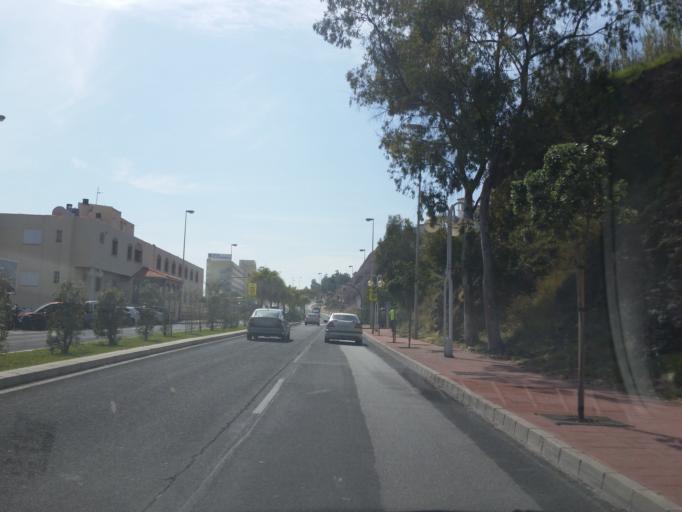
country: ES
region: Andalusia
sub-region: Provincia de Malaga
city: Benalmadena
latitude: 36.5809
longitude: -4.5586
